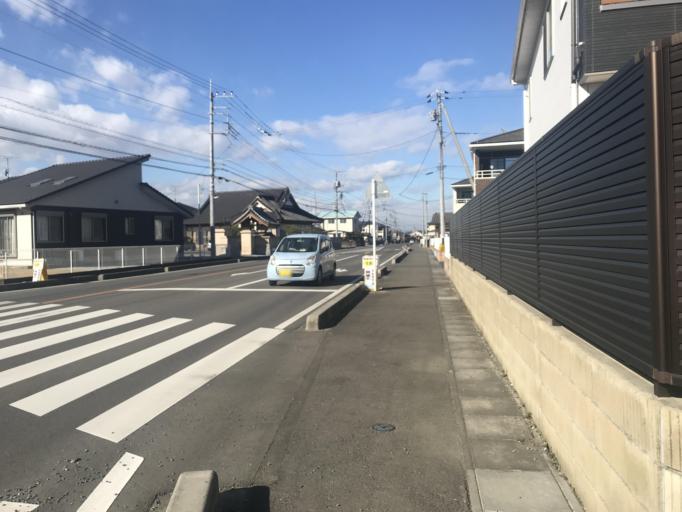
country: JP
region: Tochigi
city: Kaminokawa
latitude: 36.3762
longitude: 139.8786
